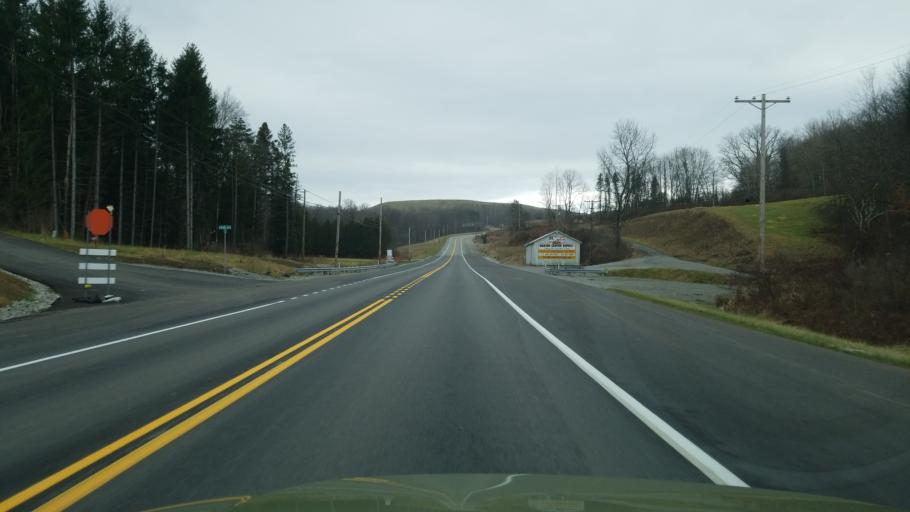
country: US
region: Pennsylvania
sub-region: Indiana County
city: Chevy Chase Heights
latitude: 40.7102
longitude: -79.1009
